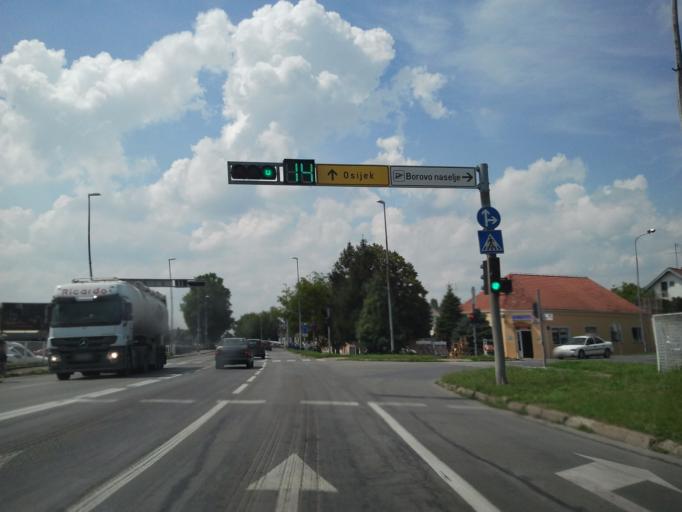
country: HR
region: Vukovarsko-Srijemska
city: Borovo
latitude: 45.3716
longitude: 18.9558
